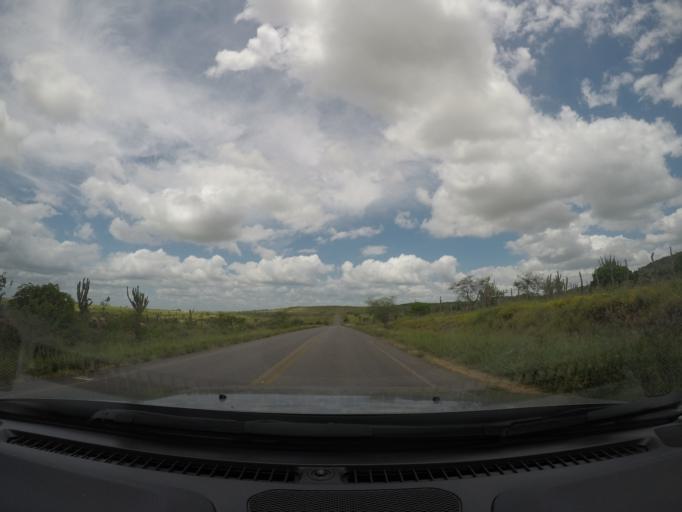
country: BR
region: Bahia
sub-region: Ipira
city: Ipira
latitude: -12.2613
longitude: -39.8282
